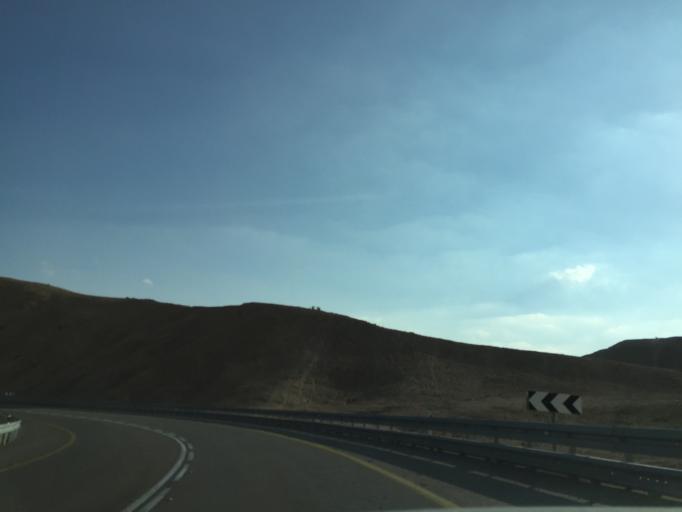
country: IL
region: Southern District
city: `En Boqeq
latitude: 31.1826
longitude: 35.2904
